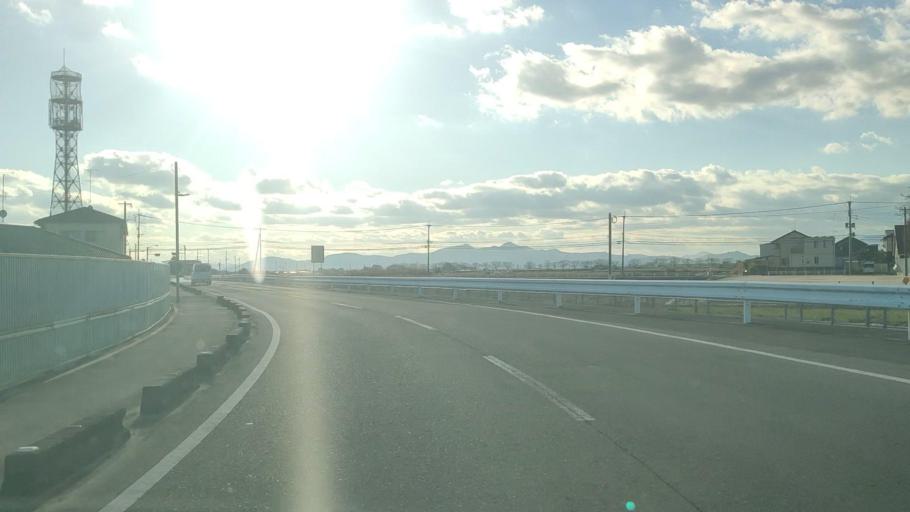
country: JP
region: Saga Prefecture
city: Saga-shi
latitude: 33.3047
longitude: 130.2558
